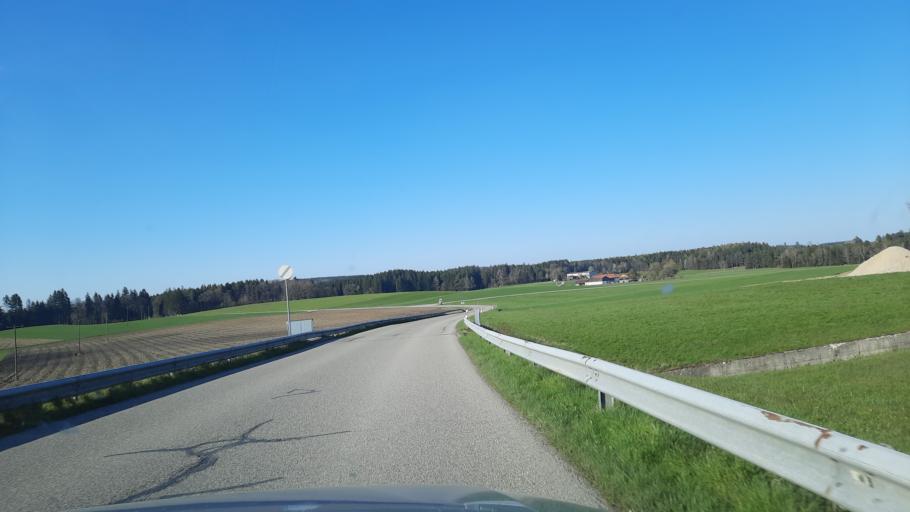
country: DE
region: Bavaria
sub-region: Upper Bavaria
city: Kirchseeon
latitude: 48.0525
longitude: 11.8971
